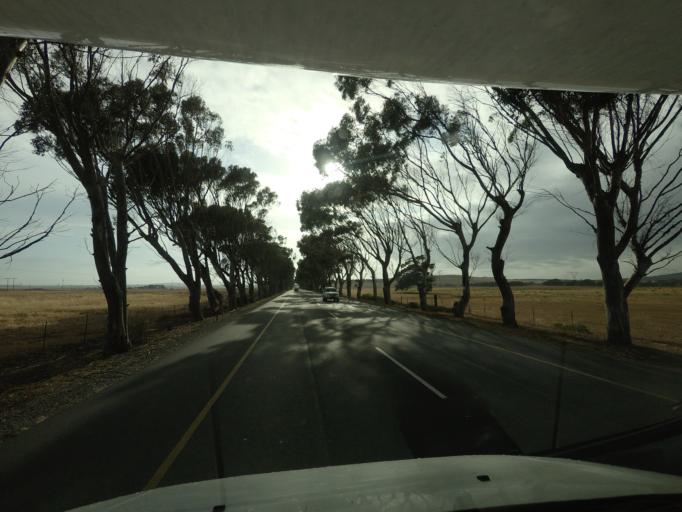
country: ZA
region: Western Cape
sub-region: City of Cape Town
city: Sunset Beach
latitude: -33.7254
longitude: 18.4649
